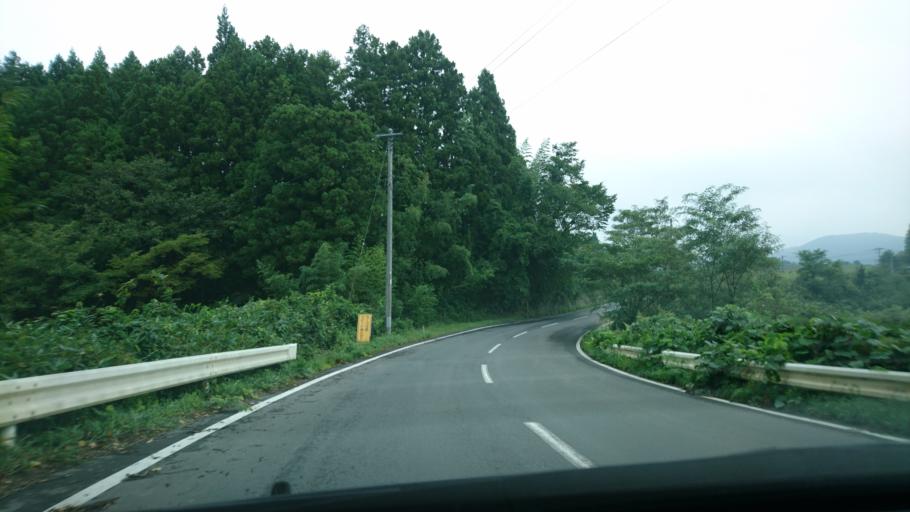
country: JP
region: Iwate
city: Ichinoseki
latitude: 38.9365
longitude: 141.1969
